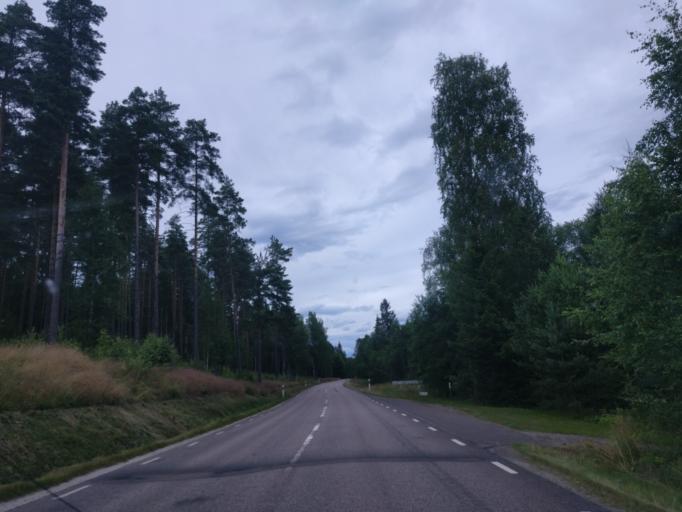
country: SE
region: Vaermland
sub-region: Hagfors Kommun
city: Ekshaerad
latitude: 60.1636
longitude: 13.4757
